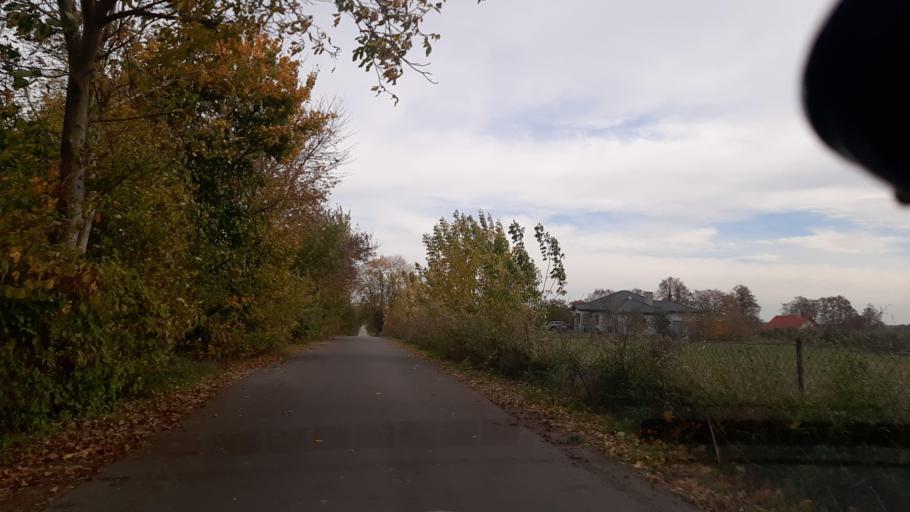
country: PL
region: Lublin Voivodeship
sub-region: Powiat pulawski
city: Naleczow
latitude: 51.3122
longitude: 22.2178
